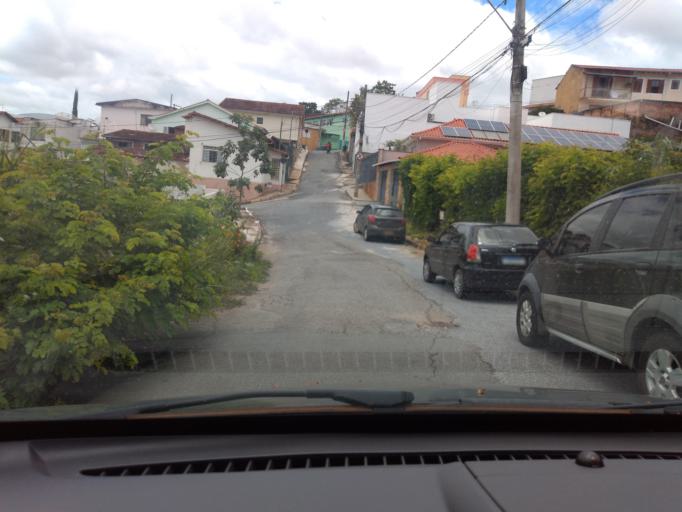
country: BR
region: Minas Gerais
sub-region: Lavras
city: Lavras
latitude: -21.2409
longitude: -44.9953
